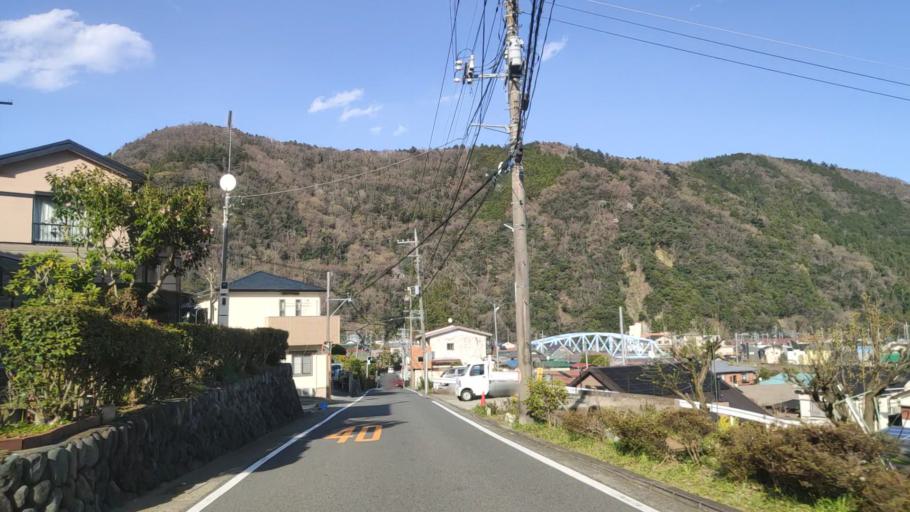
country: JP
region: Tokyo
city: Hachioji
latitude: 35.5446
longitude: 139.2624
